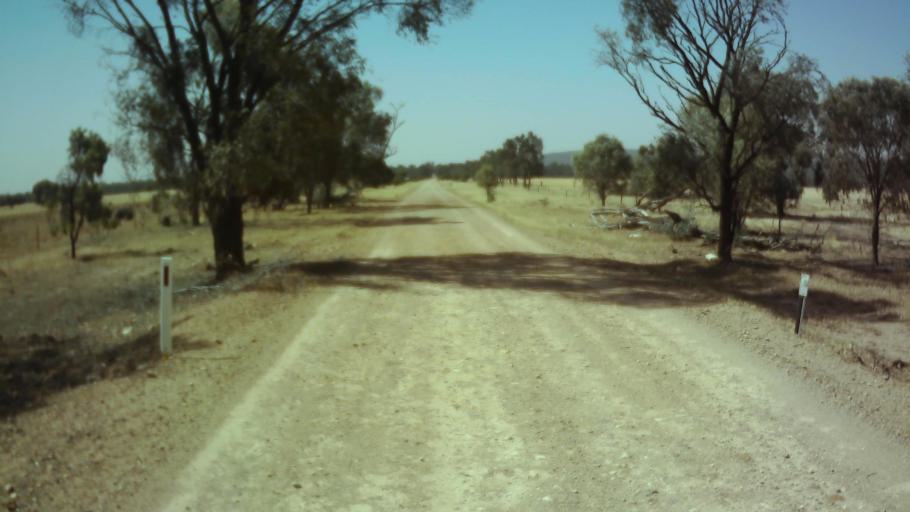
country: AU
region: New South Wales
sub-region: Weddin
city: Grenfell
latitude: -33.9865
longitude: 147.9273
